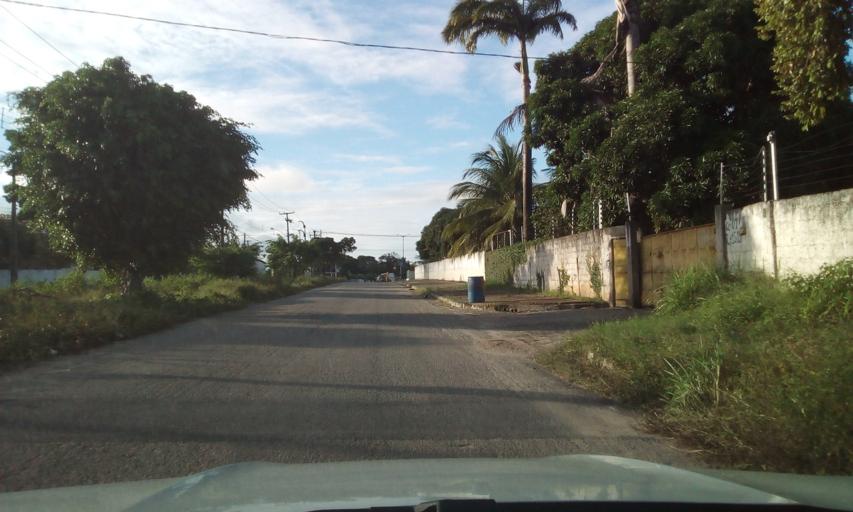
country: BR
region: Paraiba
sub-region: Joao Pessoa
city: Joao Pessoa
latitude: -7.1633
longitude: -34.8227
